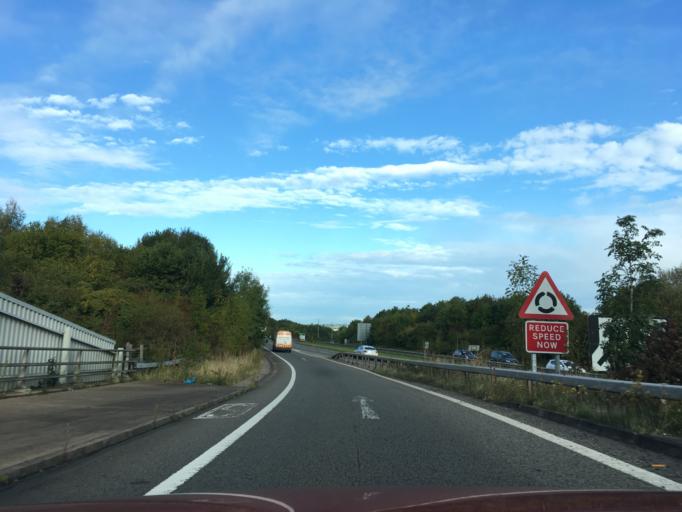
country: GB
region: England
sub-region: Gloucestershire
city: Churchdown
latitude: 51.8585
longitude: -2.1789
